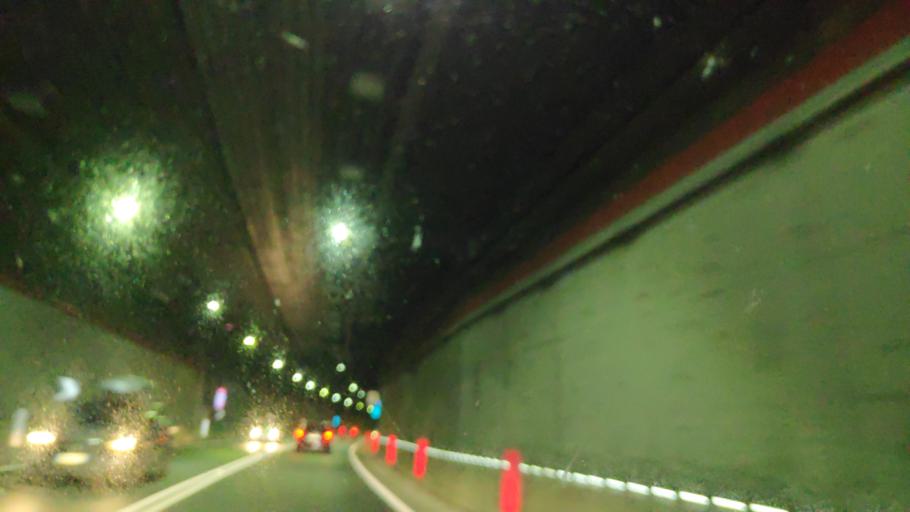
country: IT
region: Campania
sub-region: Provincia di Napoli
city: Gragnano
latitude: 40.7030
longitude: 14.5047
